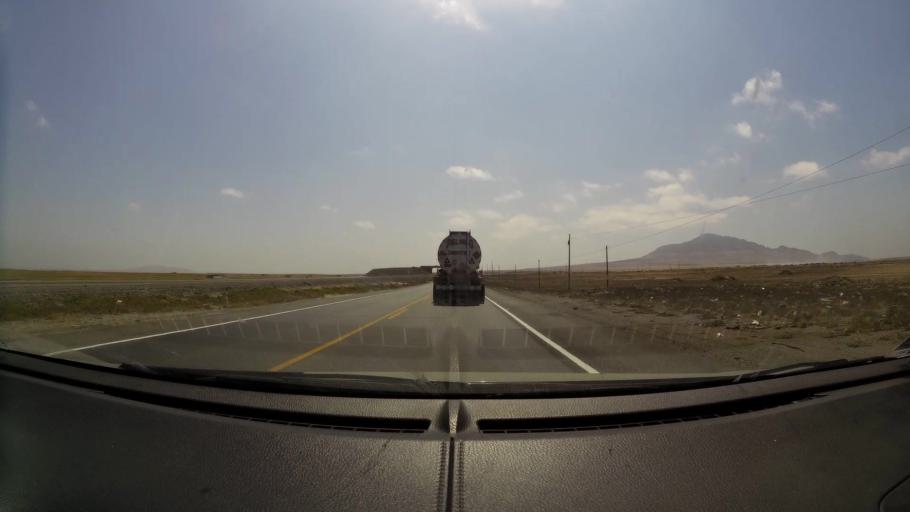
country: PE
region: Lambayeque
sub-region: Provincia de Chiclayo
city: Reque
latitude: -6.9287
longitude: -79.7397
